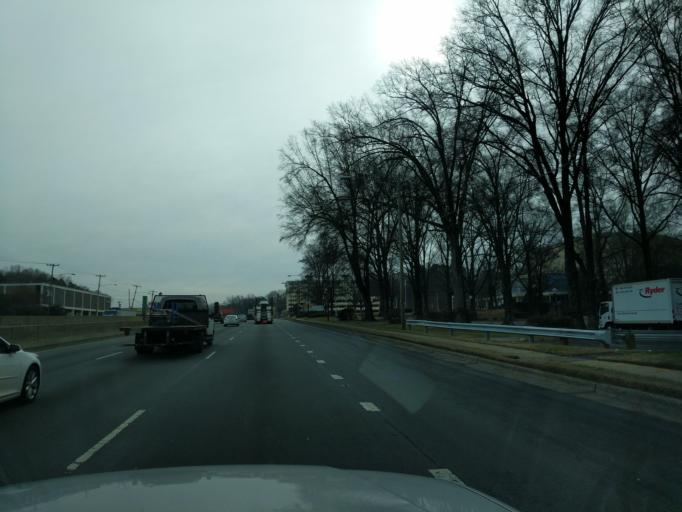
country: US
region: North Carolina
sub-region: Mecklenburg County
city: Charlotte
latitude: 35.2061
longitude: -80.7955
